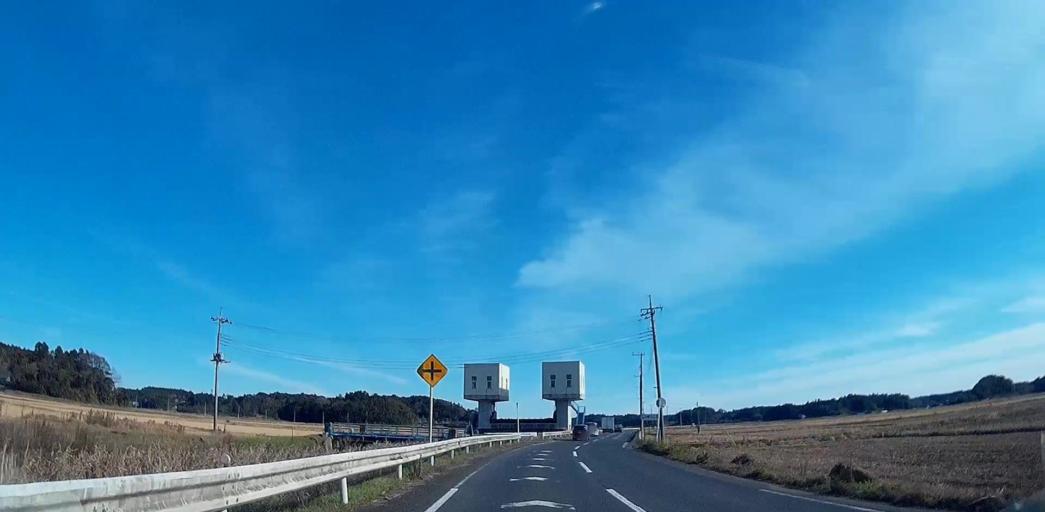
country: JP
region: Chiba
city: Yokaichiba
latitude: 35.7350
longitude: 140.5123
